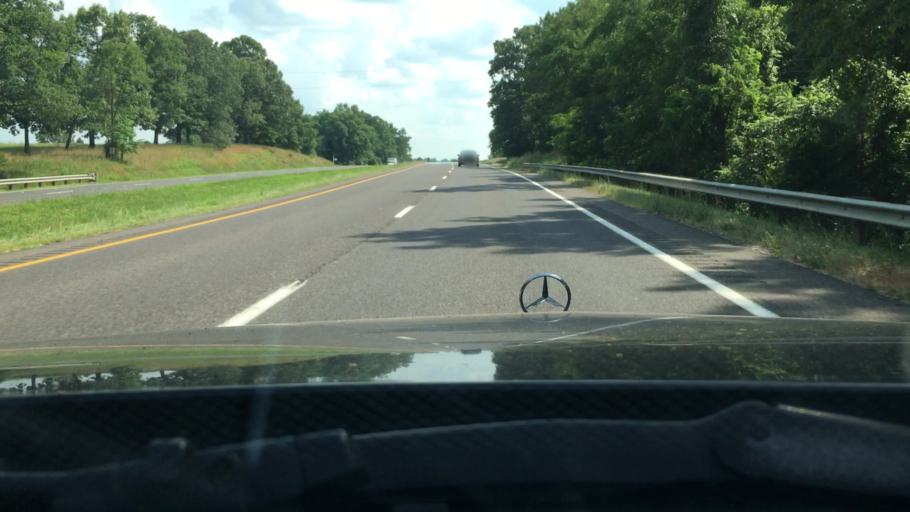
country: US
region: Virginia
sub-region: Orange County
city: Gordonsville
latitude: 38.1689
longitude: -78.1591
